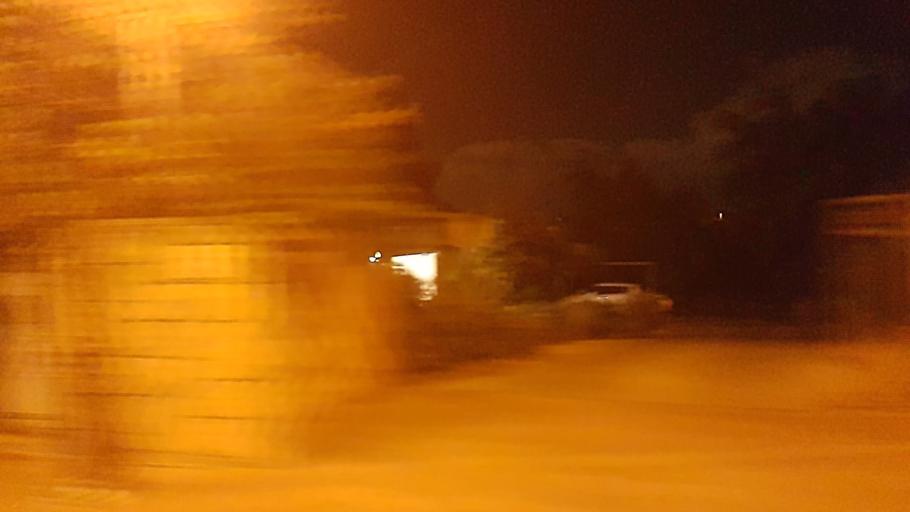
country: IL
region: Central District
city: Hod HaSharon
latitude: 32.1641
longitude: 34.8940
